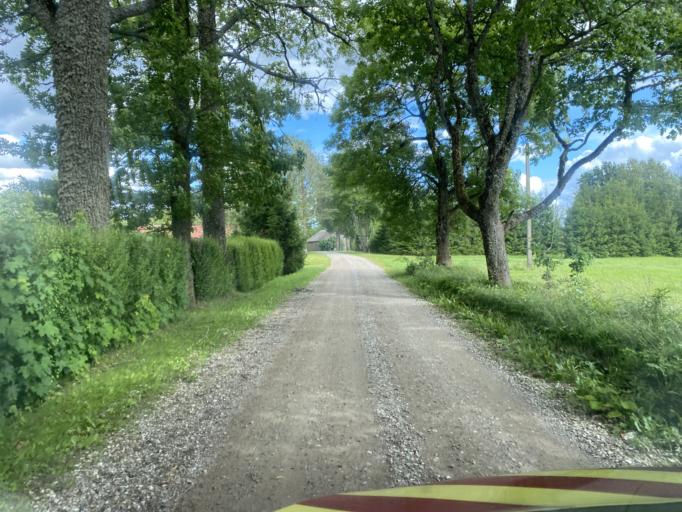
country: EE
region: Viljandimaa
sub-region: Viiratsi vald
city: Viiratsi
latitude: 58.3971
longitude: 25.8189
